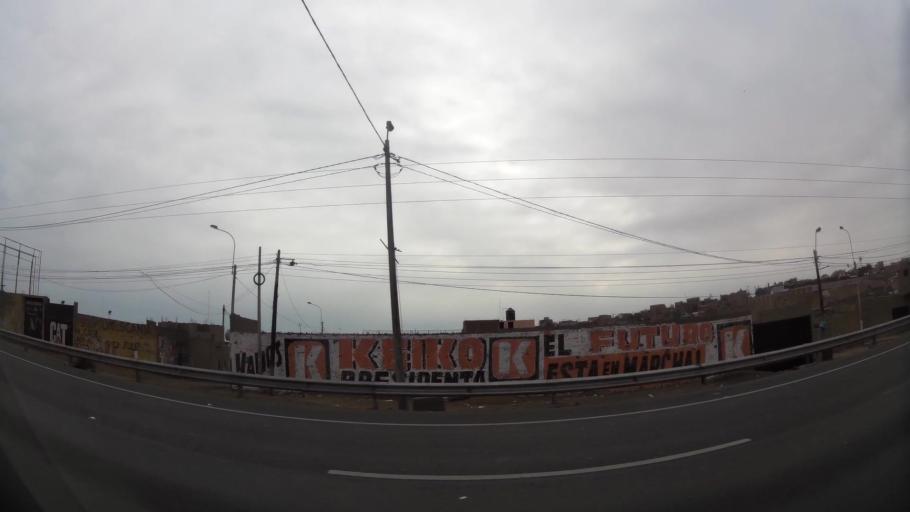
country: PE
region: Lima
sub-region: Lima
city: Surco
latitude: -12.2068
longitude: -76.9751
